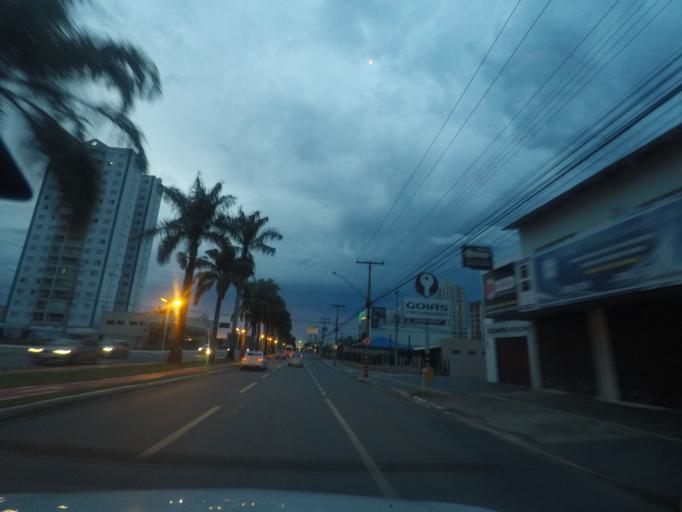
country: BR
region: Goias
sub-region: Goiania
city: Goiania
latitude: -16.7151
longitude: -49.2792
